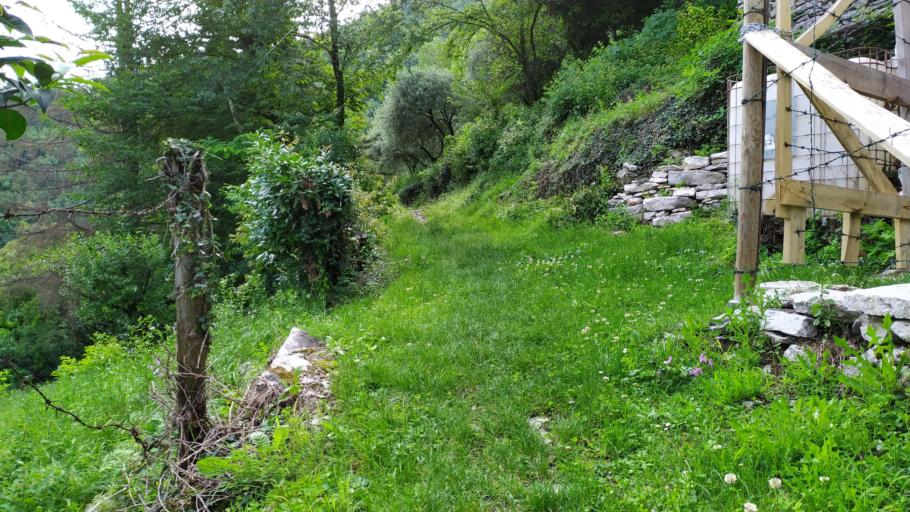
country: IT
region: Veneto
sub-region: Provincia di Vicenza
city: Torrebelvicino
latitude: 45.6954
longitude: 11.3299
